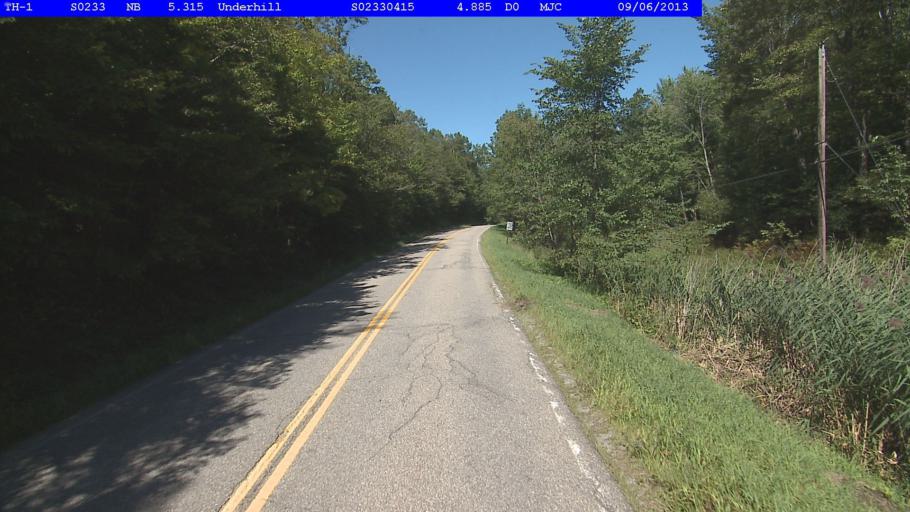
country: US
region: Vermont
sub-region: Chittenden County
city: Jericho
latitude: 44.5364
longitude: -72.8736
